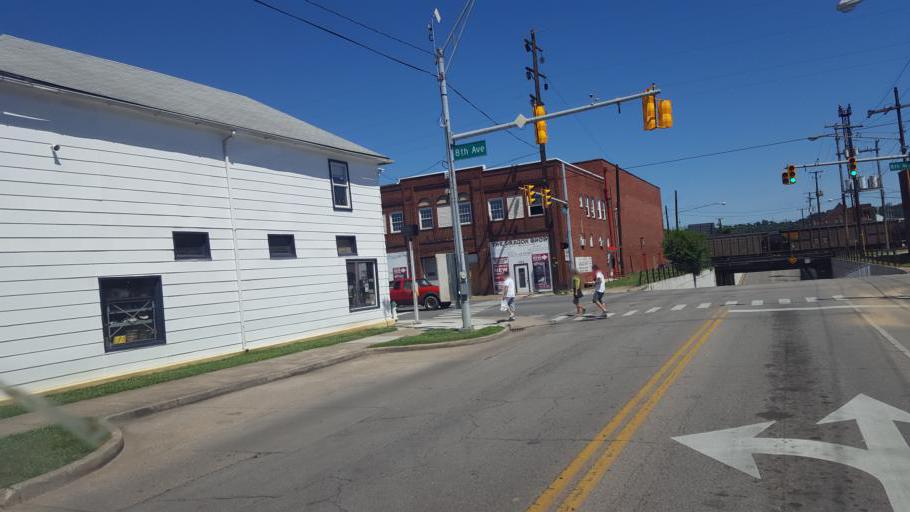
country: US
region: West Virginia
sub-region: Cabell County
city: Huntington
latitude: 38.4184
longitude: -82.4212
